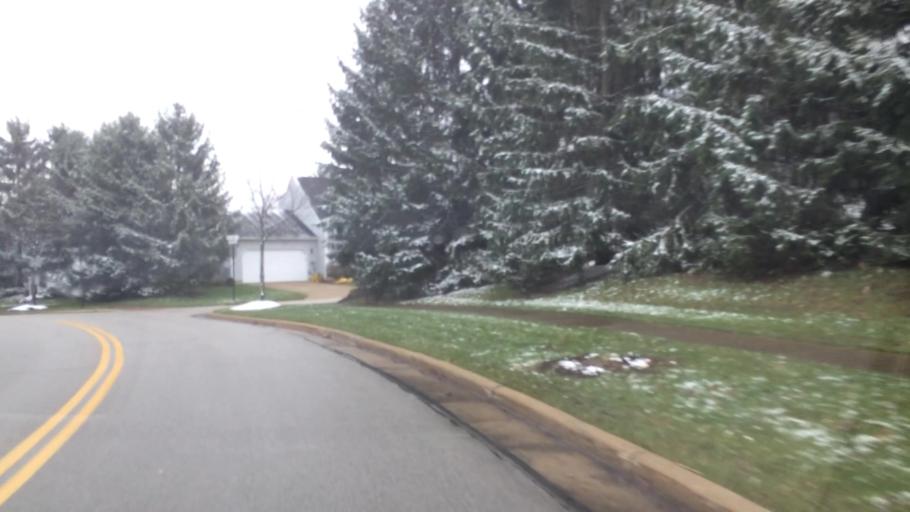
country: US
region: Ohio
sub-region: Summit County
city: Twinsburg
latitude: 41.3140
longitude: -81.4465
